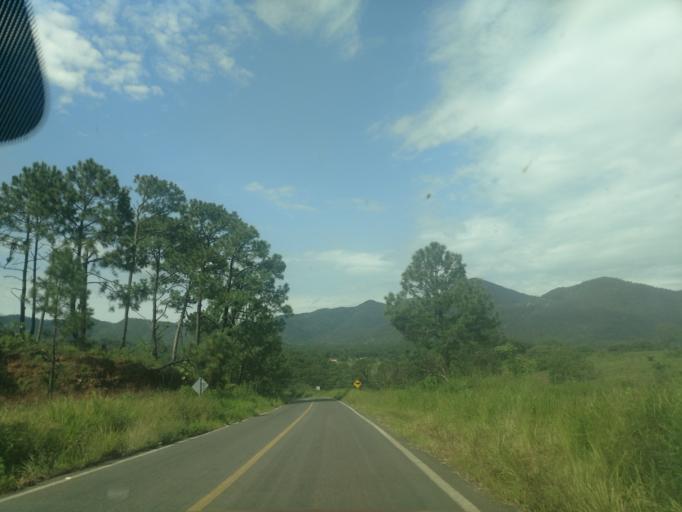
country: MX
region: Jalisco
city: Mascota
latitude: 20.4447
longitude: -104.7616
